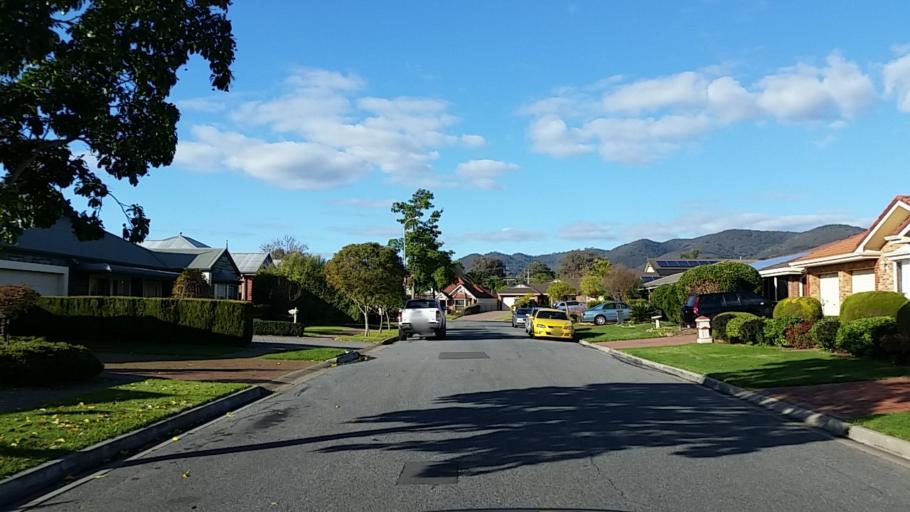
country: AU
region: South Australia
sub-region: Campbelltown
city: Paradise
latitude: -34.8733
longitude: 138.6802
